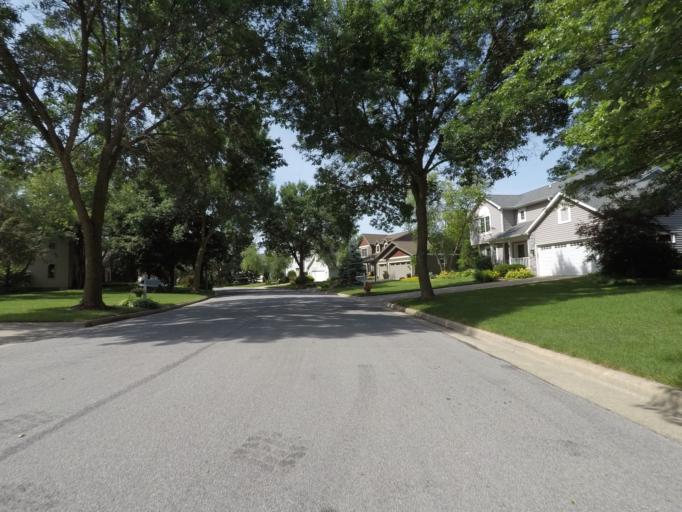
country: US
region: Wisconsin
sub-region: Dane County
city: Middleton
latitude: 43.0832
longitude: -89.5173
